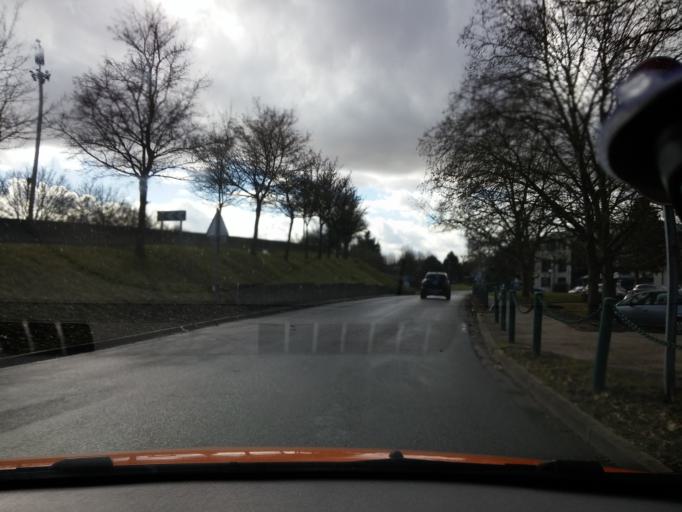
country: FR
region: Ile-de-France
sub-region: Departement de l'Essonne
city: Orsay
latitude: 48.6853
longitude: 2.2057
